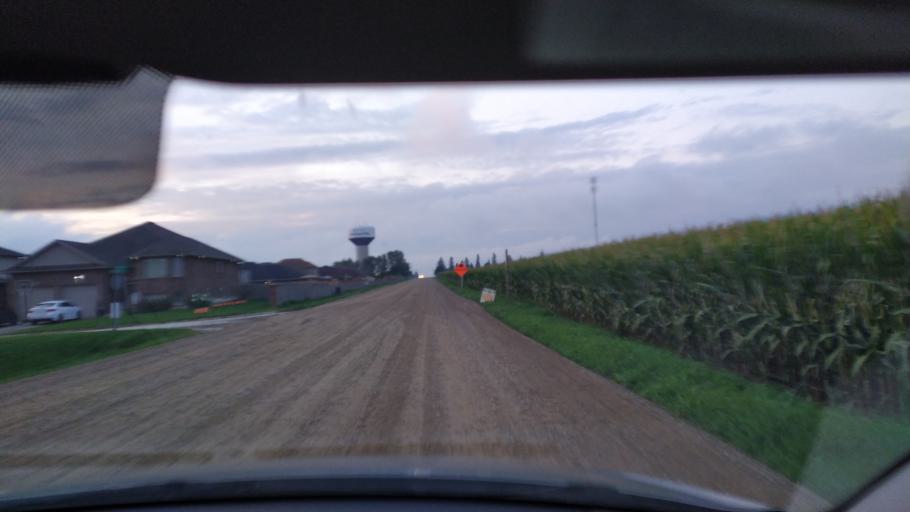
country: CA
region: Ontario
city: Kitchener
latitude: 43.3079
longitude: -80.6105
